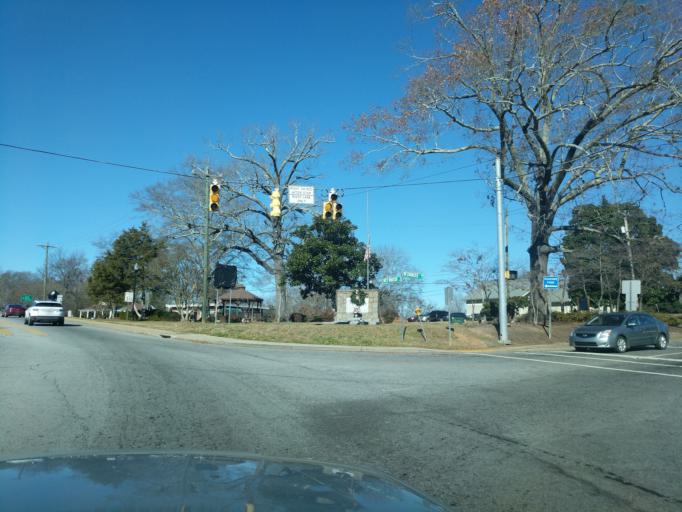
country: US
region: South Carolina
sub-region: Oconee County
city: Westminster
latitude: 34.6689
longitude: -83.1005
